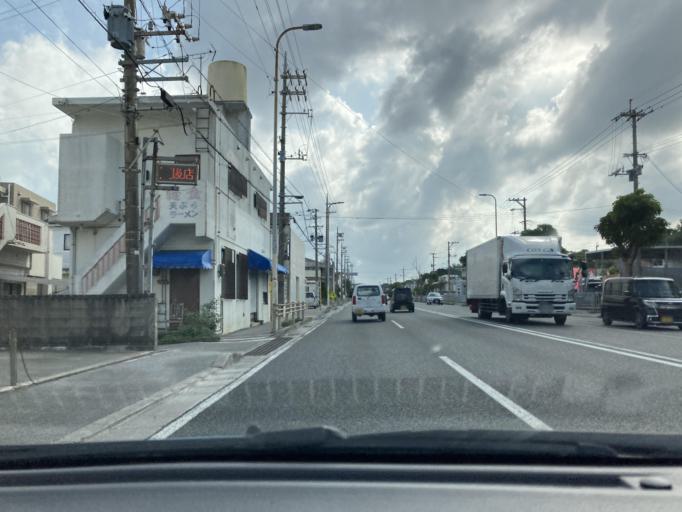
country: JP
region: Okinawa
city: Ginowan
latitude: 26.2419
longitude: 127.7790
